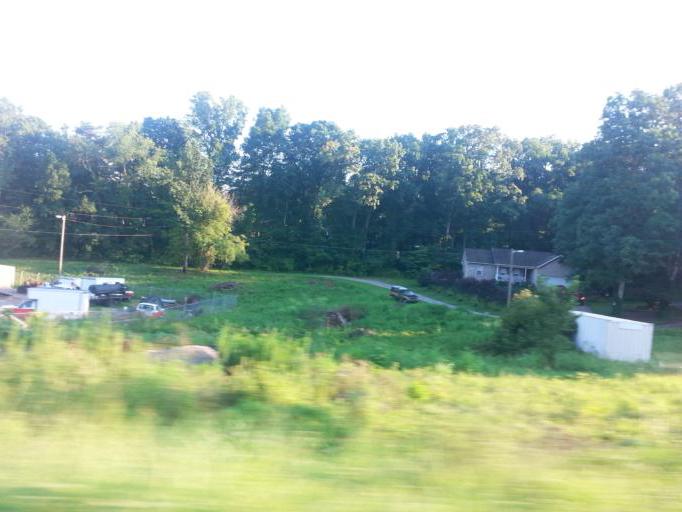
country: US
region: Tennessee
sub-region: Anderson County
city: Clinton
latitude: 36.0291
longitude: -84.0676
